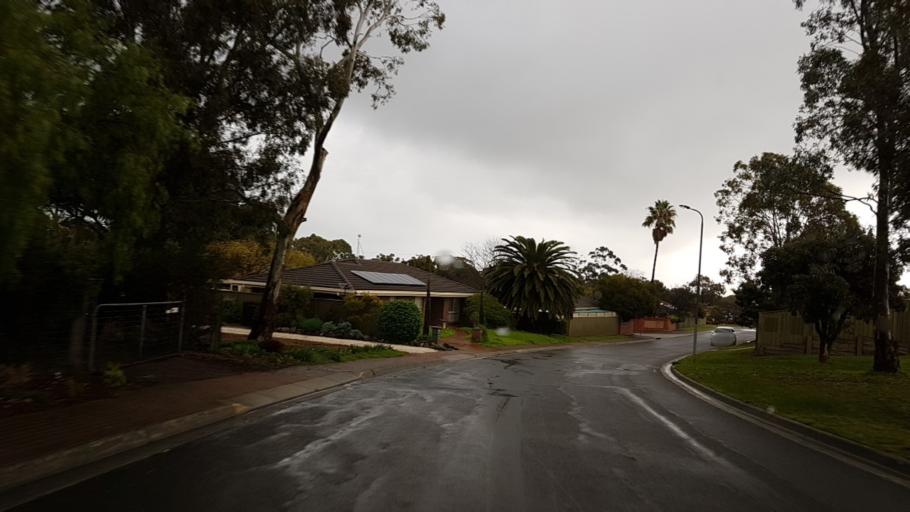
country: AU
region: South Australia
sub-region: Onkaparinga
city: Craigburn Farm
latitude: -35.0860
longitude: 138.5893
